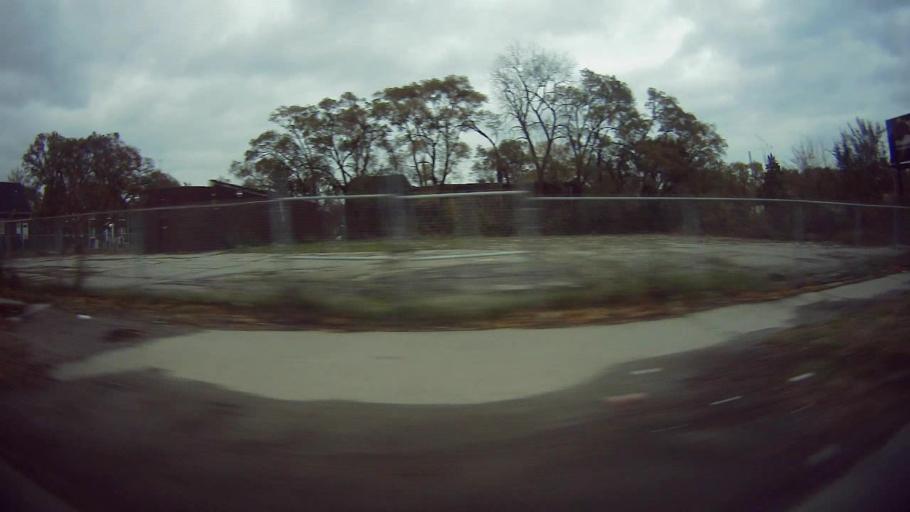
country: US
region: Michigan
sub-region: Wayne County
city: Hamtramck
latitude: 42.4020
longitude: -82.9940
